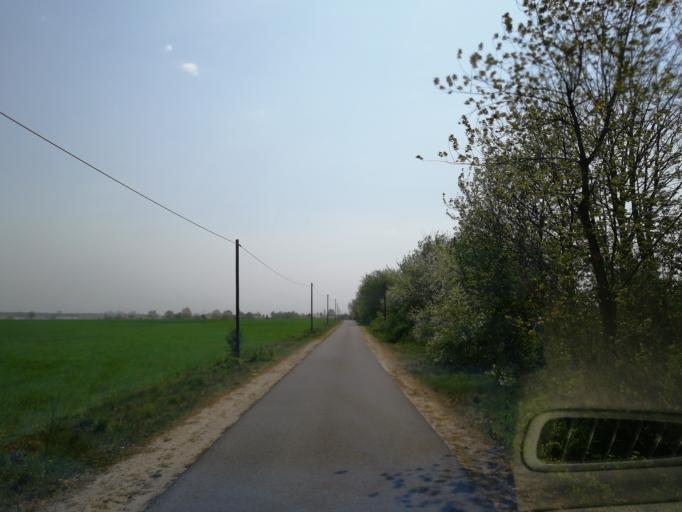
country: DE
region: Brandenburg
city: Sallgast
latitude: 51.6471
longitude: 13.8591
